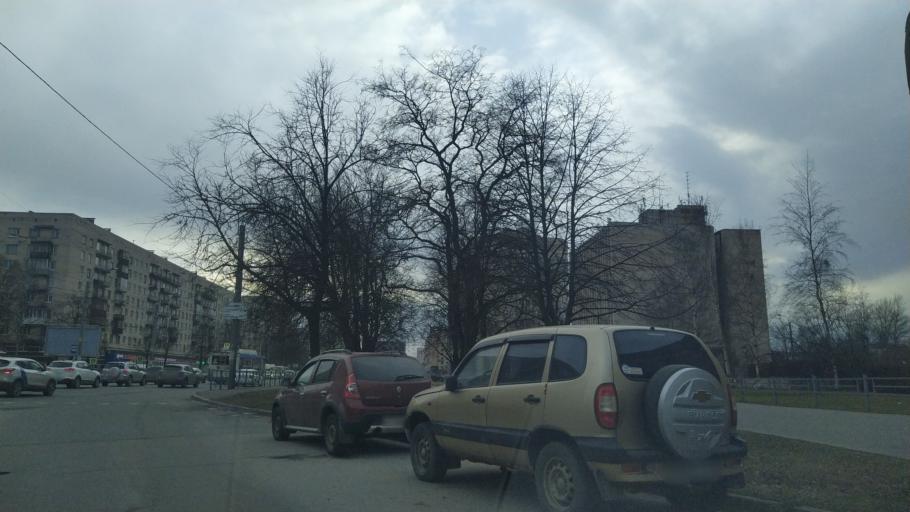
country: RU
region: Leningrad
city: Akademicheskoe
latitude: 60.0074
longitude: 30.3916
